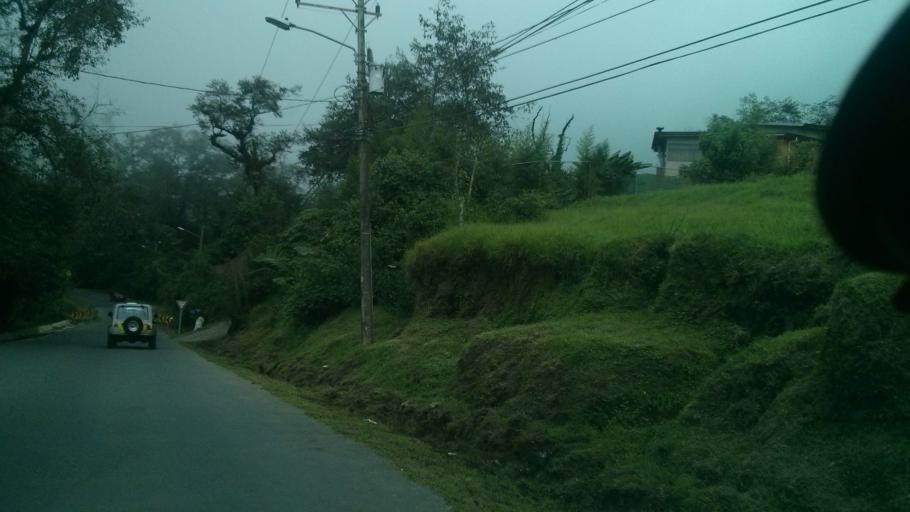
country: CR
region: San Jose
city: Ipis
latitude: 9.9999
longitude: -83.9582
